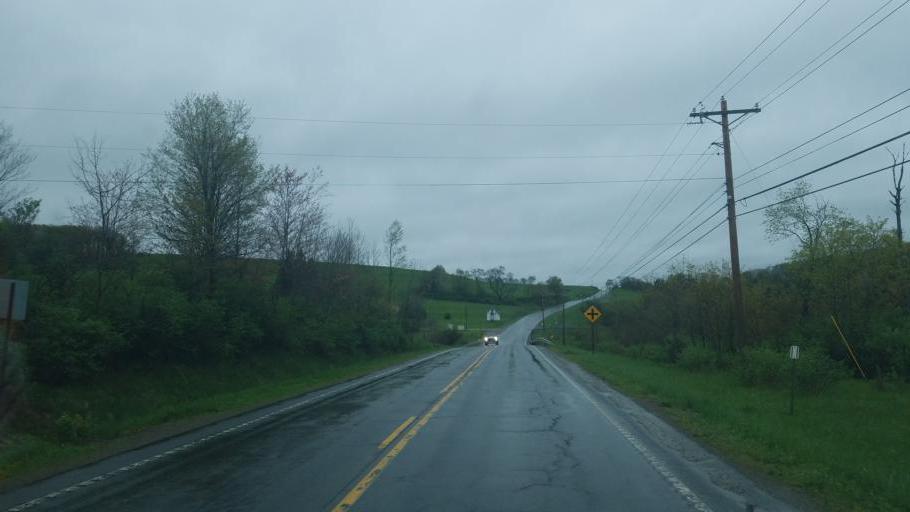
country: US
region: Pennsylvania
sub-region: Potter County
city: Galeton
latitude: 41.8892
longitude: -77.7960
